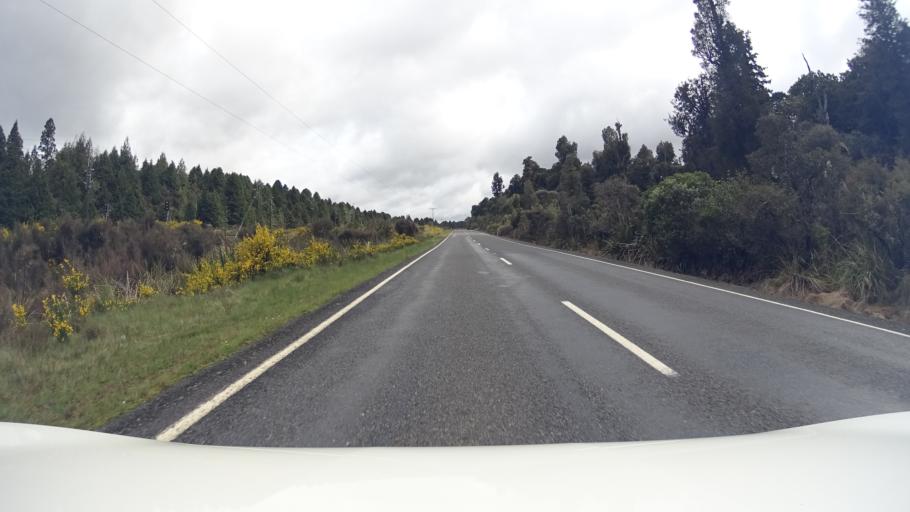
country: NZ
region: Manawatu-Wanganui
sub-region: Ruapehu District
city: Waiouru
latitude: -39.2521
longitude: 175.3882
